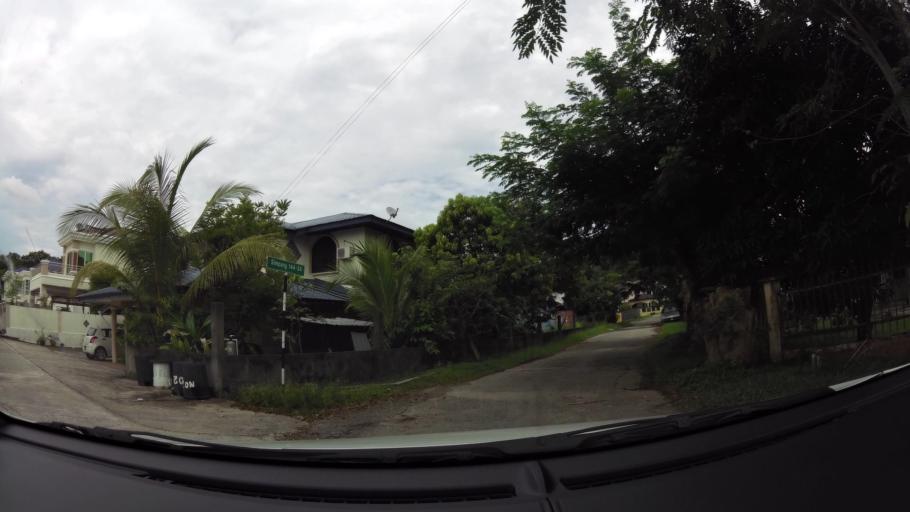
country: BN
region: Brunei and Muara
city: Bandar Seri Begawan
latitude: 4.8881
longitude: 114.9057
